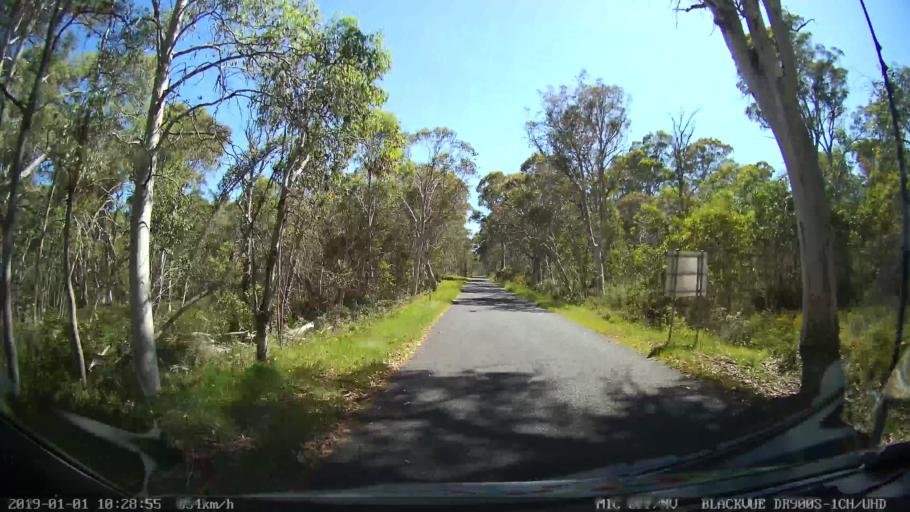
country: AU
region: New South Wales
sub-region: Snowy River
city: Jindabyne
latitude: -36.0576
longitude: 148.2441
